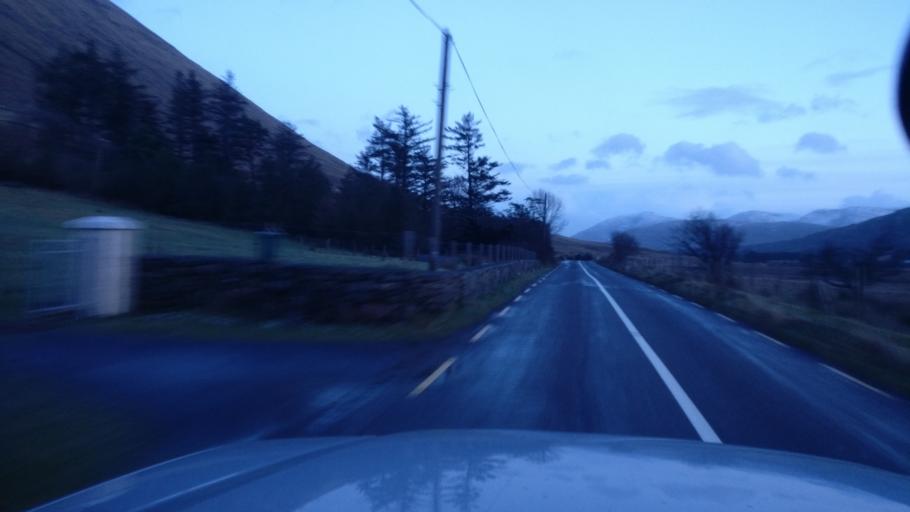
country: IE
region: Connaught
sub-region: Maigh Eo
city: Westport
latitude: 53.5674
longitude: -9.6535
